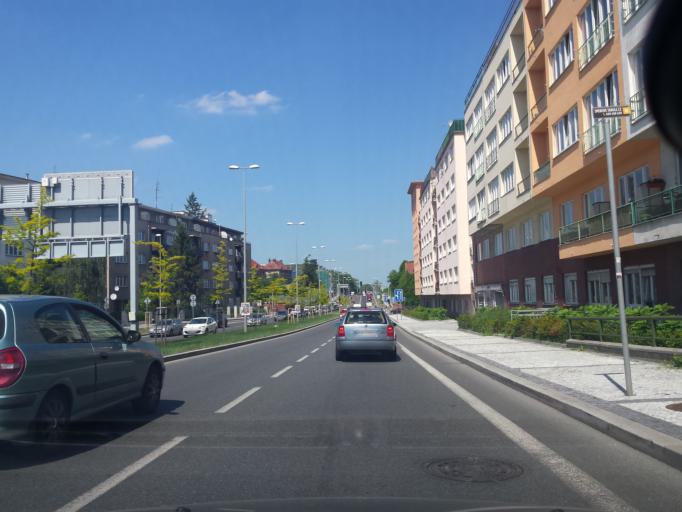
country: CZ
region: Praha
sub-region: Praha 1
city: Mala Strana
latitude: 50.0892
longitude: 14.3833
